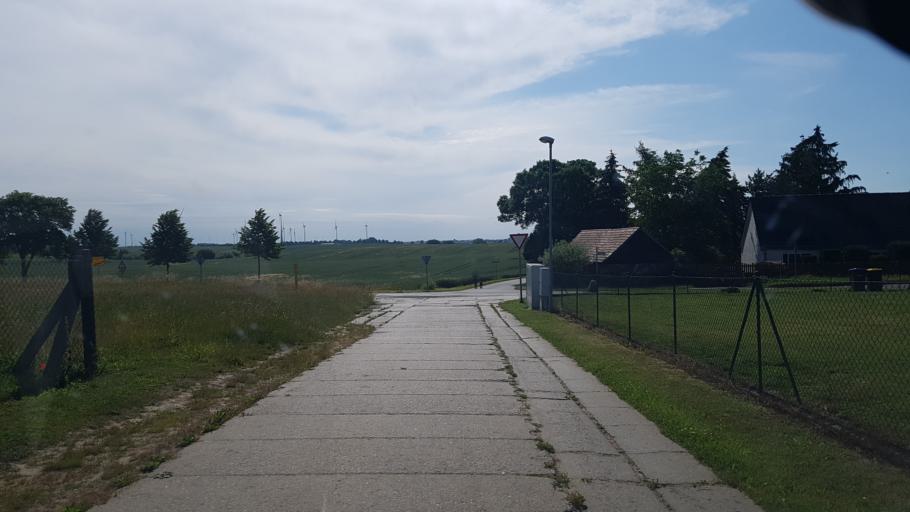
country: DE
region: Brandenburg
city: Gramzow
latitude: 53.2608
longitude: 13.9768
